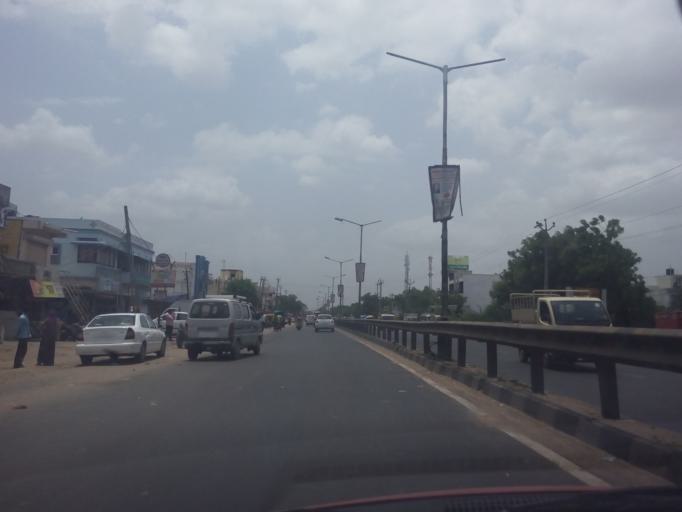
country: IN
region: Gujarat
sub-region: Ahmadabad
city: Sanand
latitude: 22.9890
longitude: 72.3813
